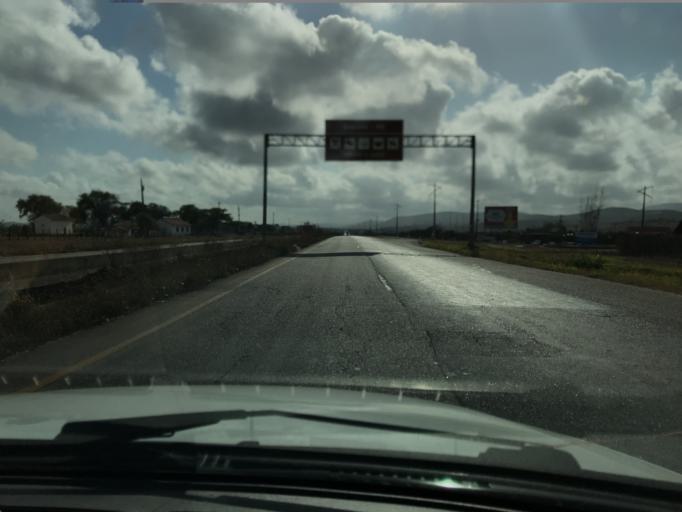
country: BR
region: Pernambuco
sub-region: Gravata
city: Gravata
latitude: -8.2166
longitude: -35.6488
